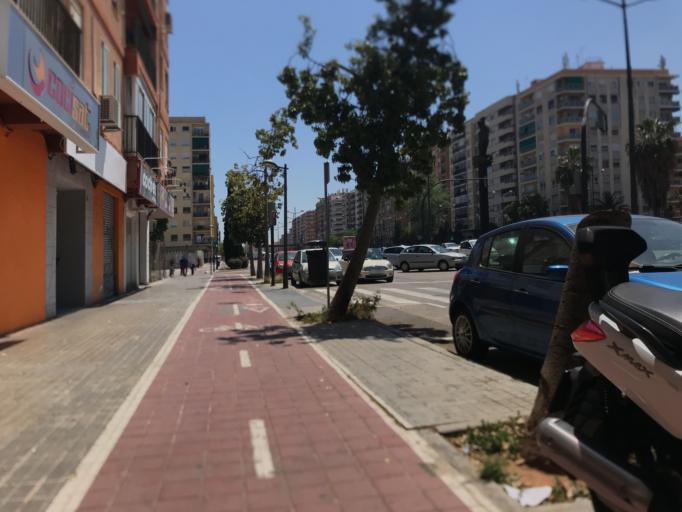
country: ES
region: Valencia
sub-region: Provincia de Valencia
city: Valencia
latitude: 39.4534
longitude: -0.3730
